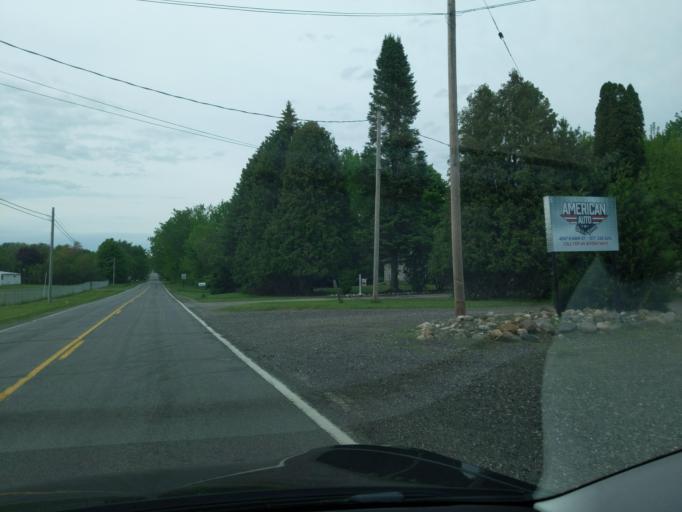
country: US
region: Michigan
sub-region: Ingham County
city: Leslie
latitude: 42.4594
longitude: -84.4358
